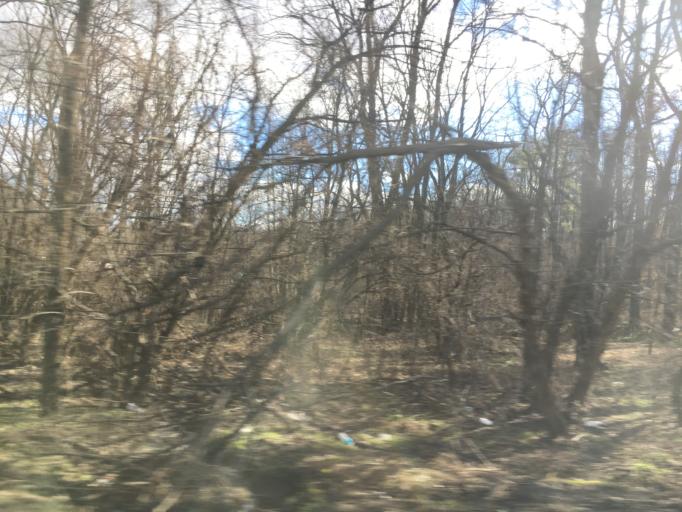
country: US
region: Pennsylvania
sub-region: Lehigh County
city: Egypt
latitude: 40.6736
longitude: -75.5262
